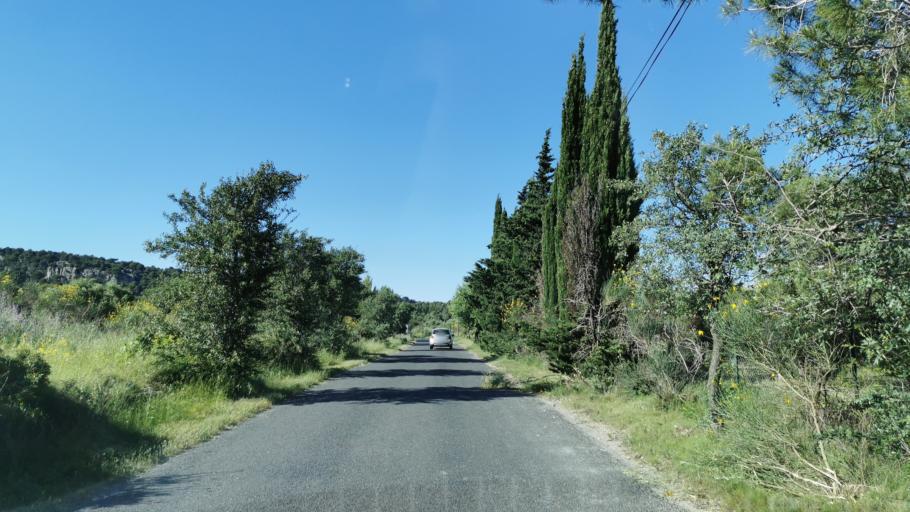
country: FR
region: Languedoc-Roussillon
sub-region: Departement de l'Aude
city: Gruissan
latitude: 43.1210
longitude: 3.0947
